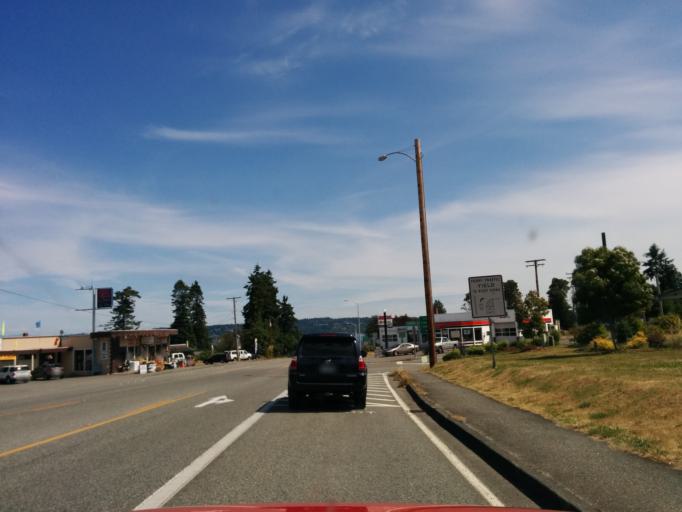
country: US
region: Washington
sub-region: Snohomish County
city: Mukilteo
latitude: 47.9784
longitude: -122.3559
